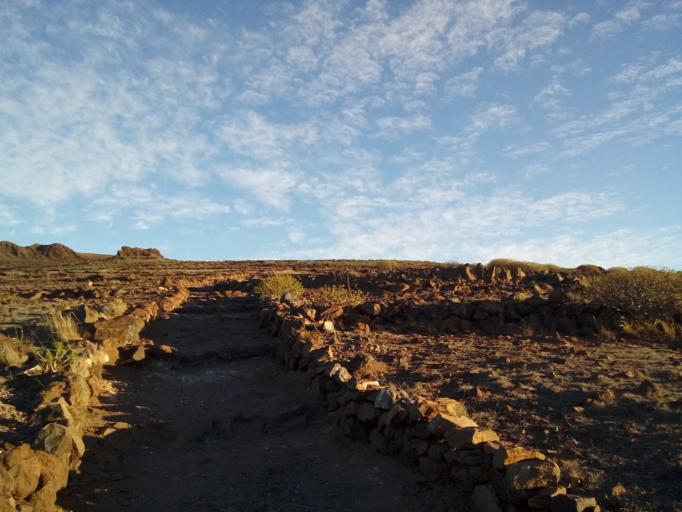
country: ES
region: Canary Islands
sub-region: Provincia de Santa Cruz de Tenerife
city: Vallehermosa
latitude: 28.1072
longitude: -17.3364
